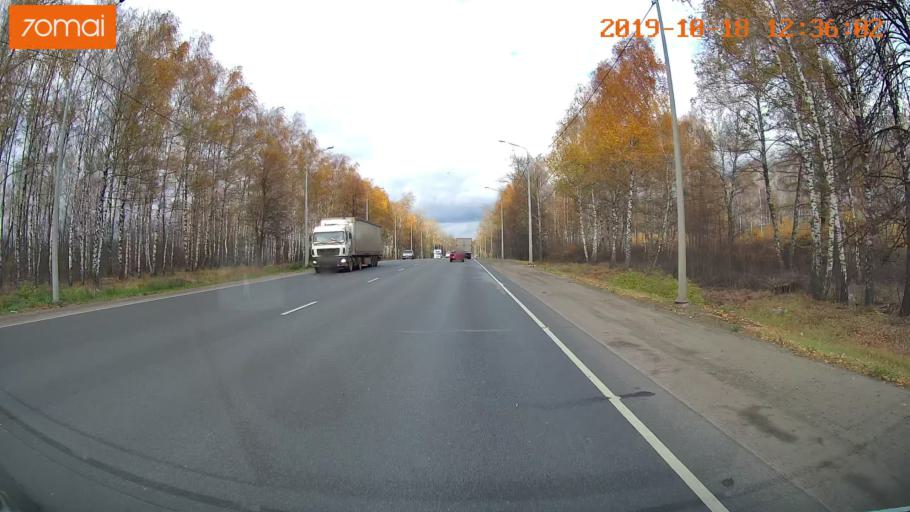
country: RU
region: Rjazan
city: Ryazan'
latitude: 54.6308
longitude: 39.6346
